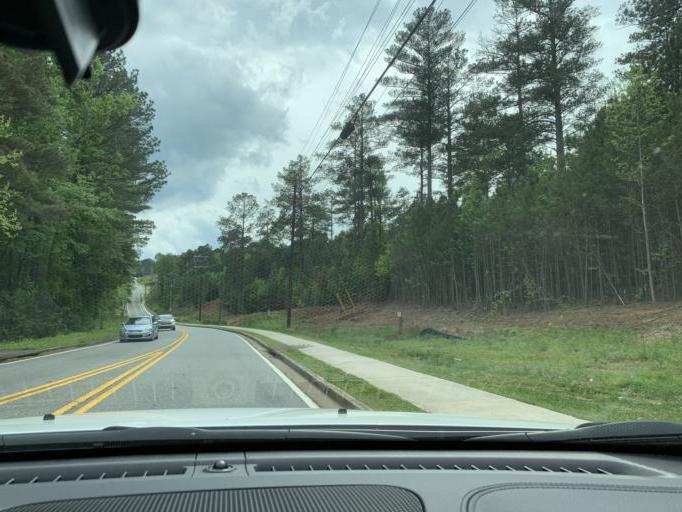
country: US
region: Georgia
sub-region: Gwinnett County
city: Sugar Hill
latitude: 34.1271
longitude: -84.1013
